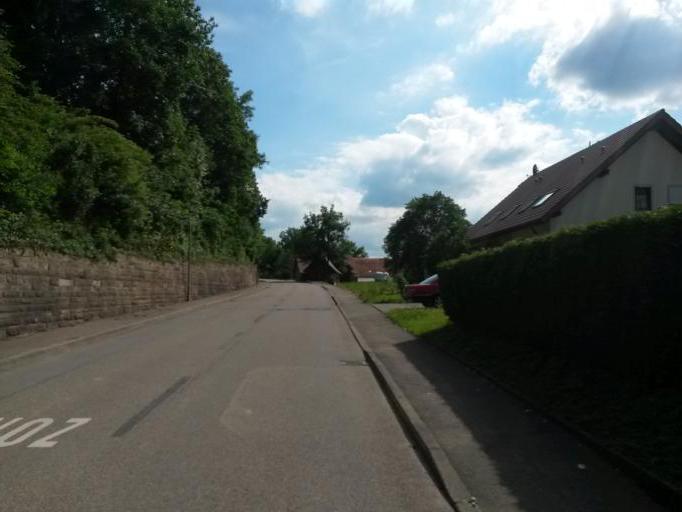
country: DE
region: Baden-Wuerttemberg
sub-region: Karlsruhe Region
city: Konigsbach-Stein
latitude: 48.9284
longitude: 8.5717
